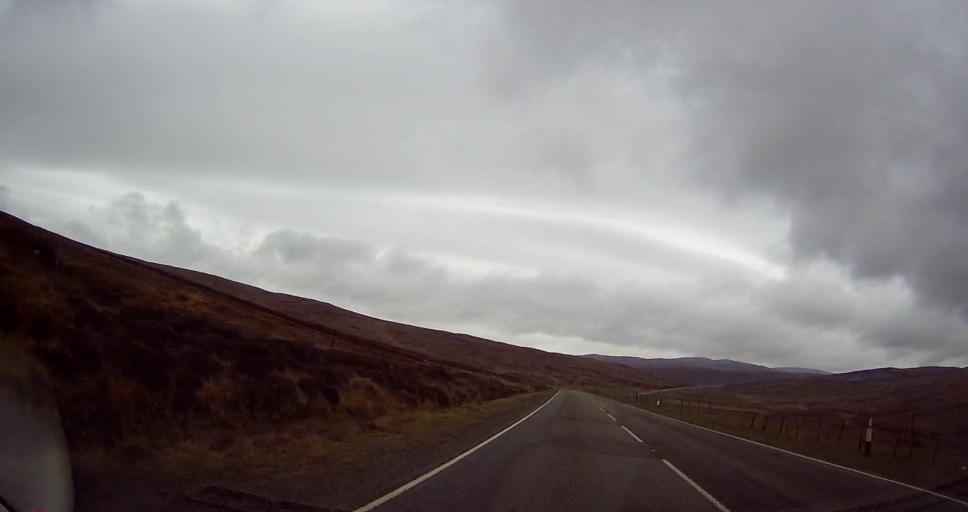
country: GB
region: Scotland
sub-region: Shetland Islands
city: Lerwick
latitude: 60.2662
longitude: -1.2245
